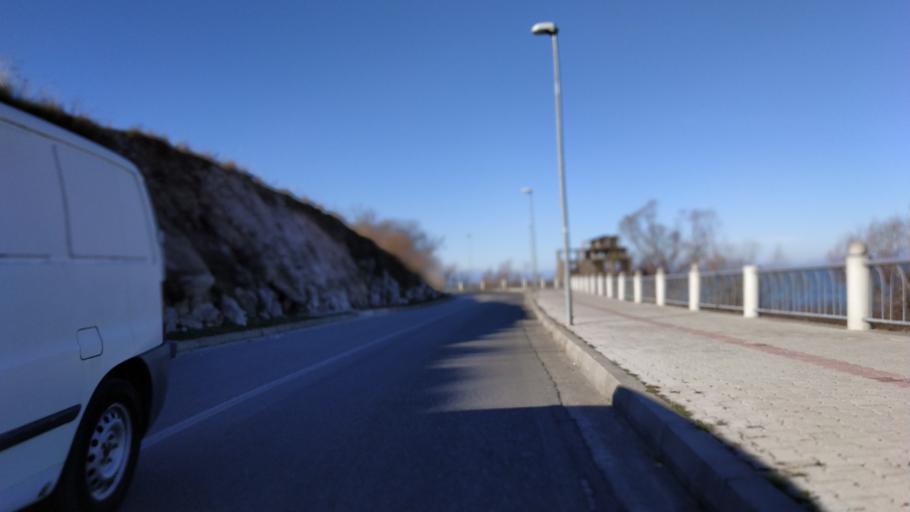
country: AL
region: Shkoder
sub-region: Rrethi i Shkodres
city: Berdica e Madhe
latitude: 42.0580
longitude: 19.4635
